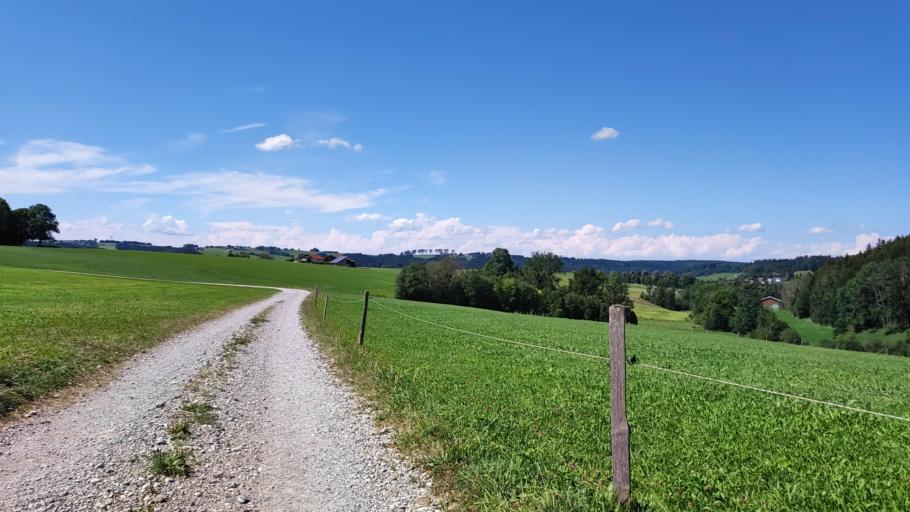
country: DE
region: Bavaria
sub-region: Swabia
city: Obergunzburg
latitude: 47.8400
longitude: 10.4350
